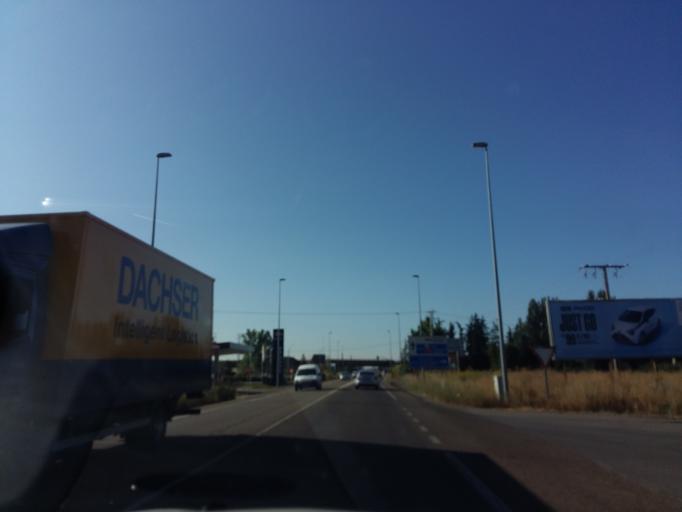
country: ES
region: Castille and Leon
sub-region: Provincia de Leon
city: Leon
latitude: 42.5721
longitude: -5.5829
